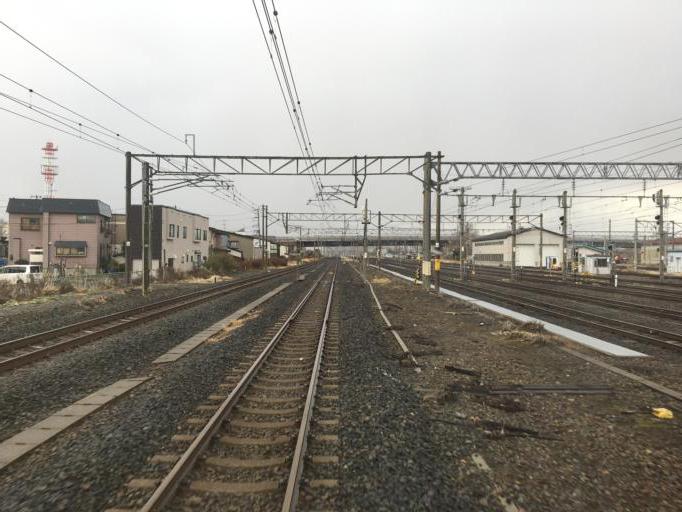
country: JP
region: Aomori
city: Aomori Shi
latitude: 40.8180
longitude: 140.7402
